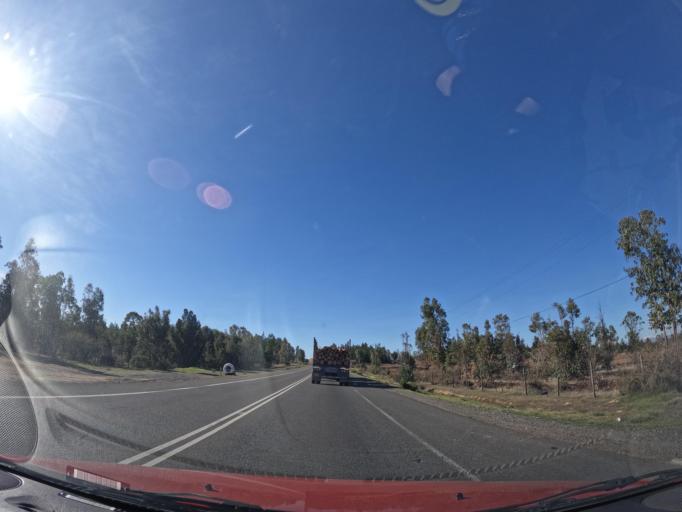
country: CL
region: Maule
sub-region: Provincia de Cauquenes
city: Cauquenes
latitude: -35.9306
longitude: -72.1887
